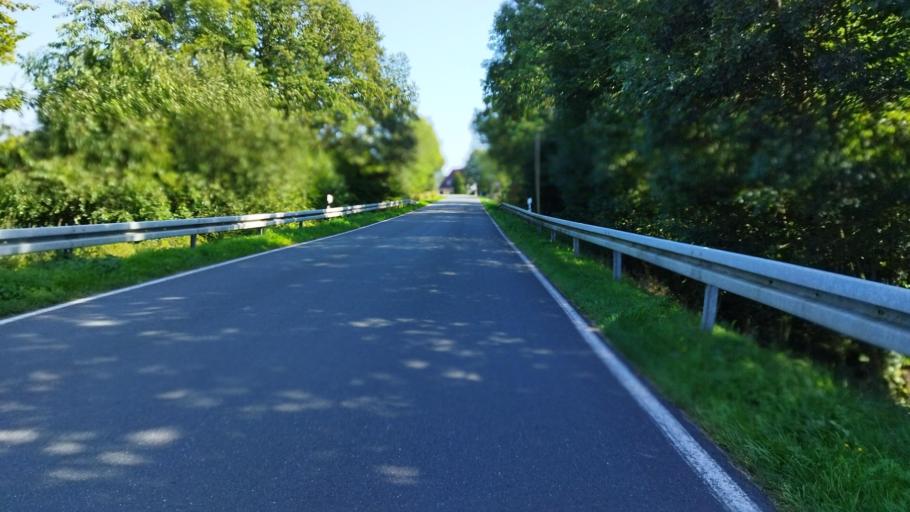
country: DE
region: North Rhine-Westphalia
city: Lengerich
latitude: 52.2289
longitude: 7.8791
